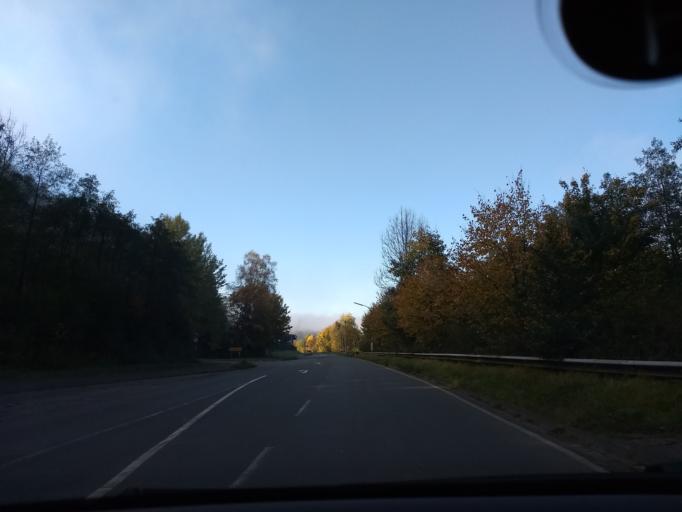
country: DE
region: North Rhine-Westphalia
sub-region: Regierungsbezirk Arnsberg
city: Finnentrop
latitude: 51.1803
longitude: 8.0136
